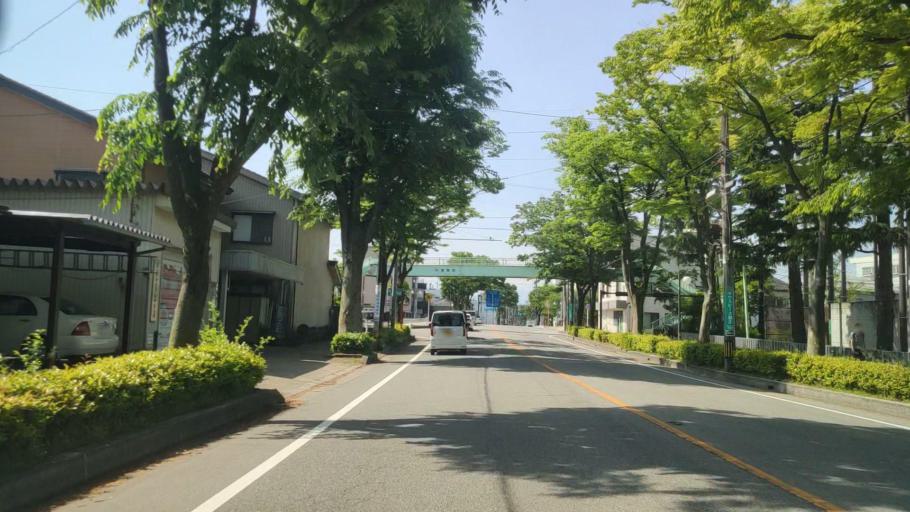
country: JP
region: Toyama
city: Toyama-shi
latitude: 36.6945
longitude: 137.2047
